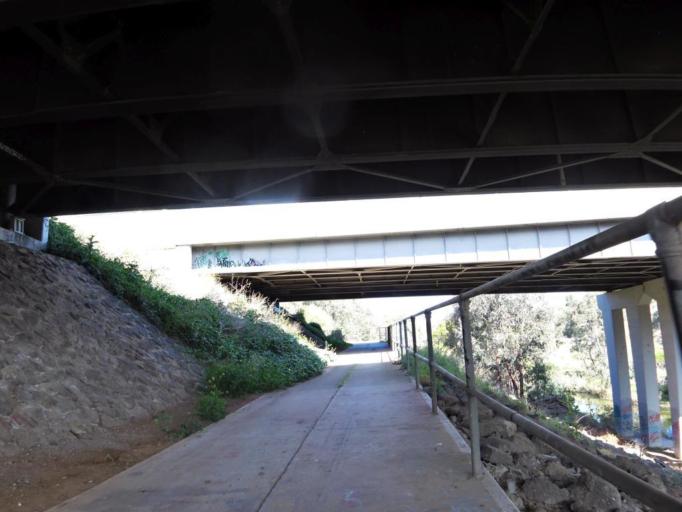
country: AU
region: Victoria
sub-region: Wyndham
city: Werribee
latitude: -37.9197
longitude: 144.6577
